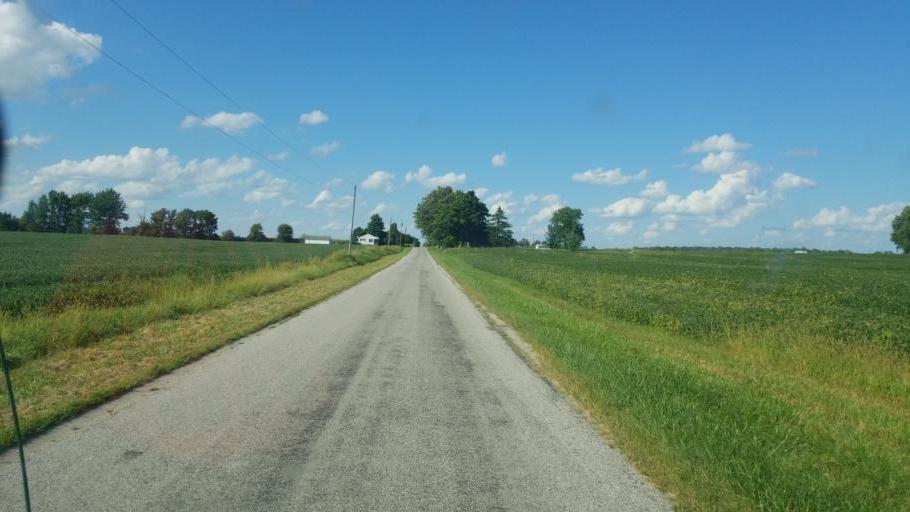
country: US
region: Ohio
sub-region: Union County
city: Richwood
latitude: 40.5900
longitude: -83.3430
